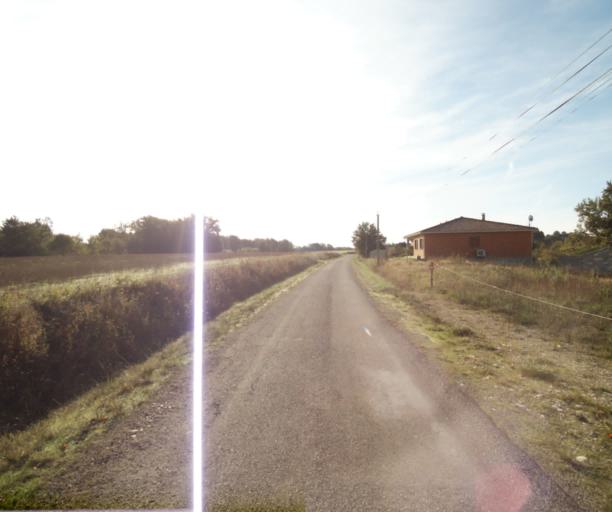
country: FR
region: Midi-Pyrenees
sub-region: Departement de la Haute-Garonne
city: Villemur-sur-Tarn
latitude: 43.9095
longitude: 1.5142
